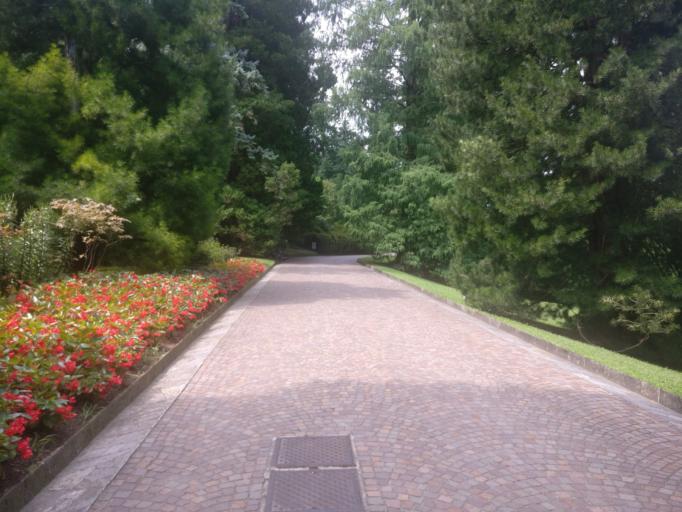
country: IT
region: Piedmont
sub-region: Provincia Verbano-Cusio-Ossola
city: Verbania
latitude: 45.9258
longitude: 8.5638
